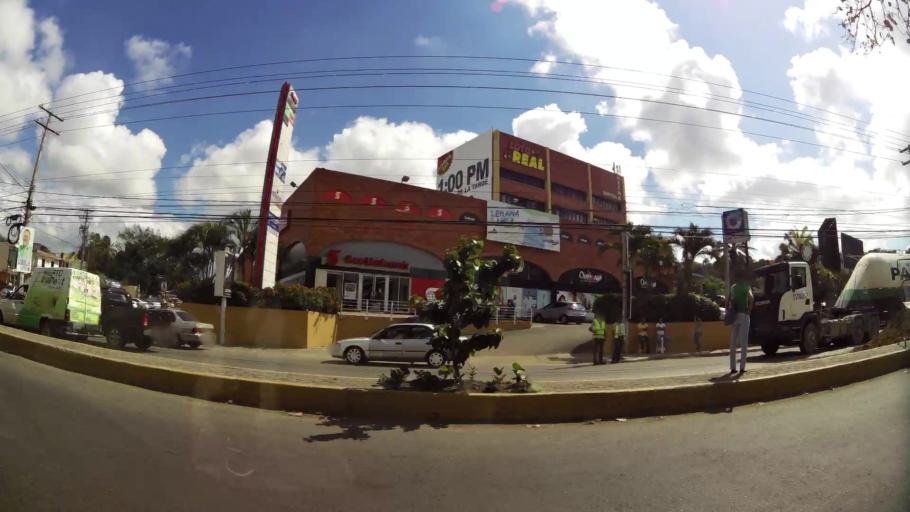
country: DO
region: Santiago
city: Santiago de los Caballeros
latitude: 19.4690
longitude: -70.6872
